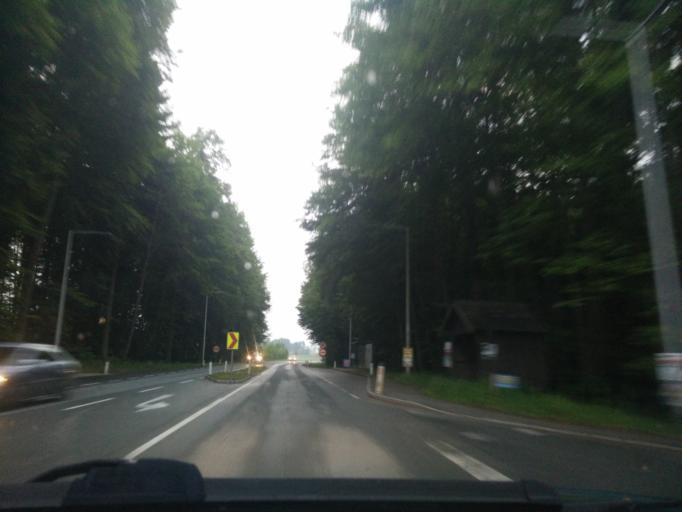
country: AT
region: Salzburg
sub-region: Politischer Bezirk Salzburg-Umgebung
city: Elixhausen
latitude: 47.8892
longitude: 13.0707
